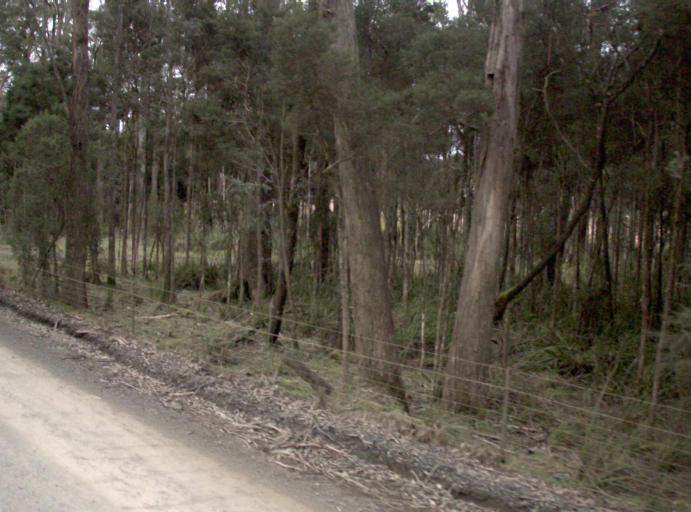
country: AU
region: Tasmania
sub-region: Launceston
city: Newstead
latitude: -41.3594
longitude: 147.2271
